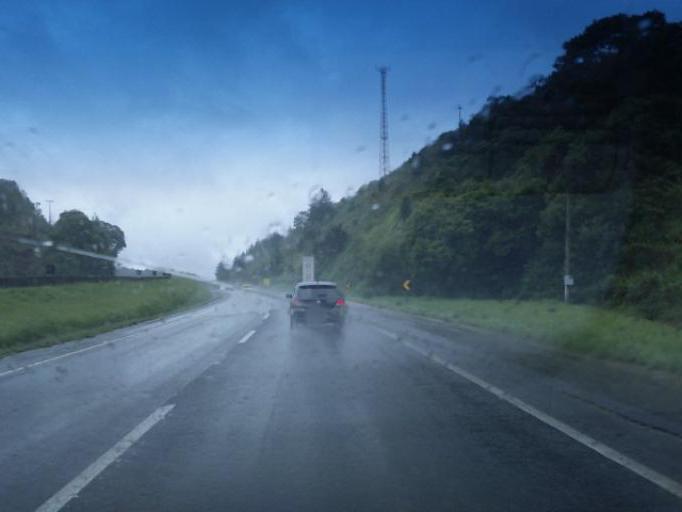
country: BR
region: Parana
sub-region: Campina Grande Do Sul
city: Campina Grande do Sul
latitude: -25.2475
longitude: -48.9053
